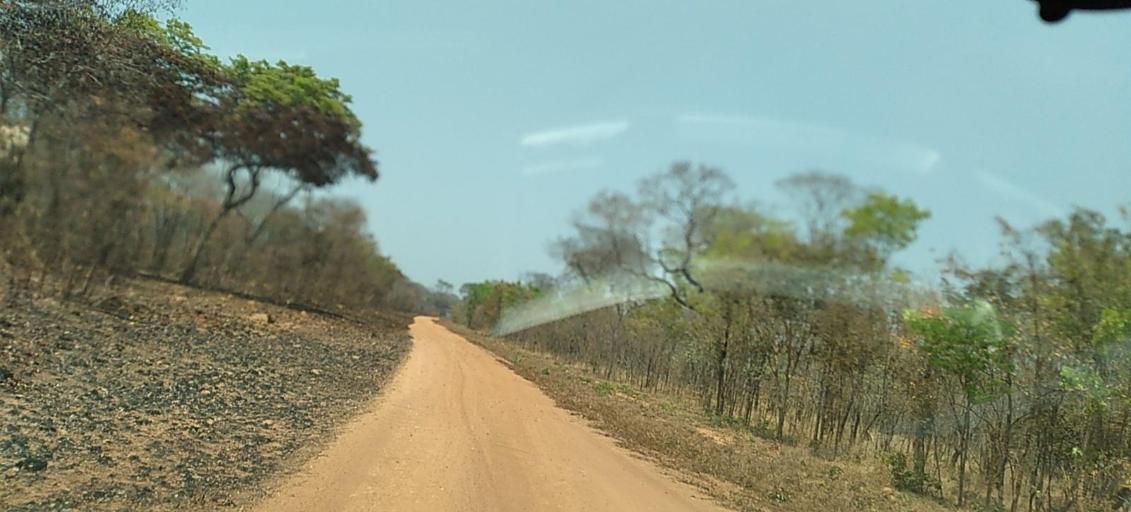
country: ZM
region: Central
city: Mumbwa
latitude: -14.3883
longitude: 26.4877
